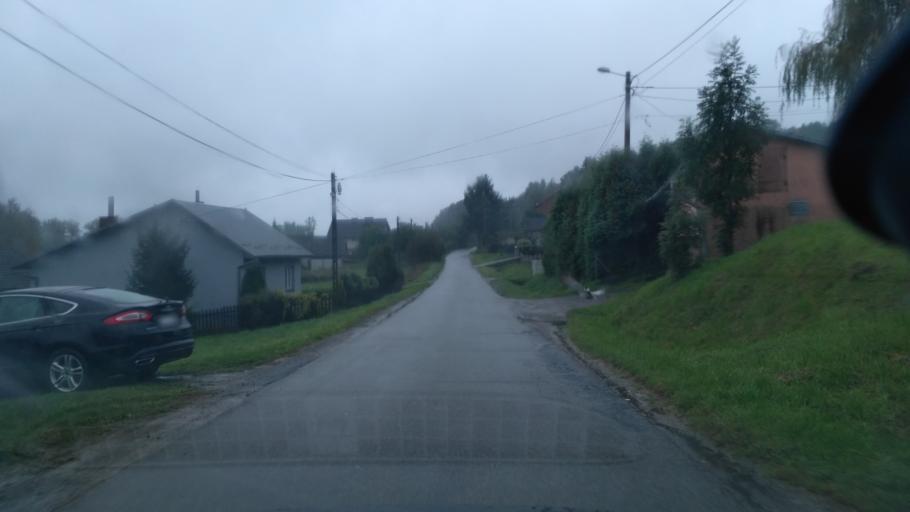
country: PL
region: Subcarpathian Voivodeship
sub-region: Powiat ropczycko-sedziszowski
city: Niedzwiada
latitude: 50.0133
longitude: 21.5473
